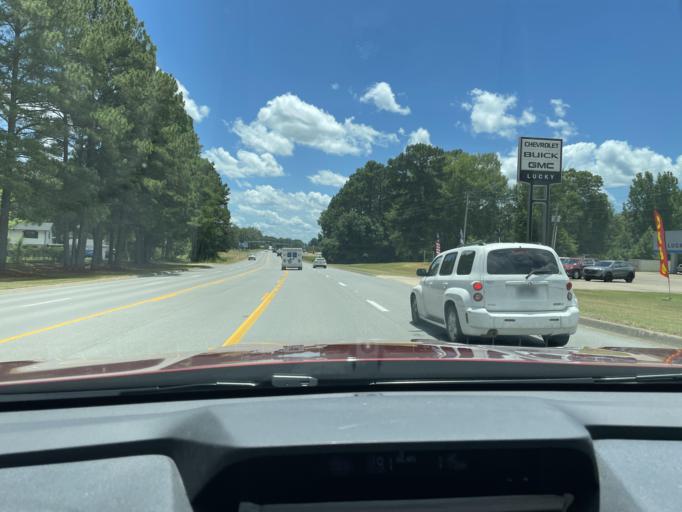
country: US
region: Arkansas
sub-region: Drew County
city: Monticello
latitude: 33.6514
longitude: -91.8023
